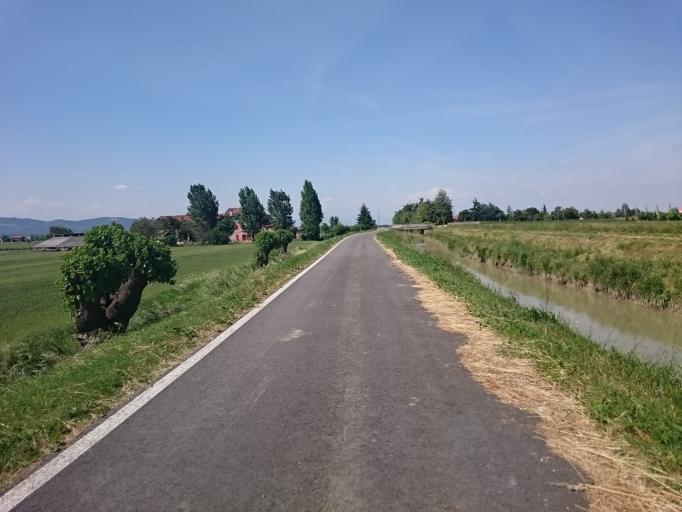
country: IT
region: Veneto
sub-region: Provincia di Padova
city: Vo
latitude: 45.3594
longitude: 11.6304
